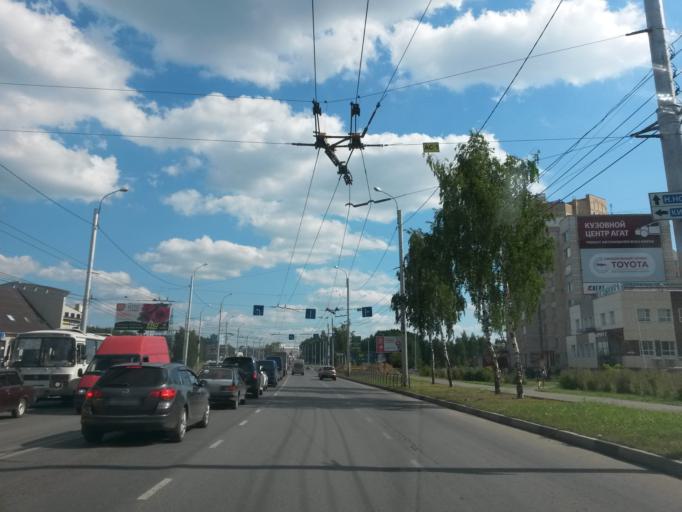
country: RU
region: Ivanovo
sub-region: Gorod Ivanovo
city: Ivanovo
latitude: 56.9620
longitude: 41.0271
